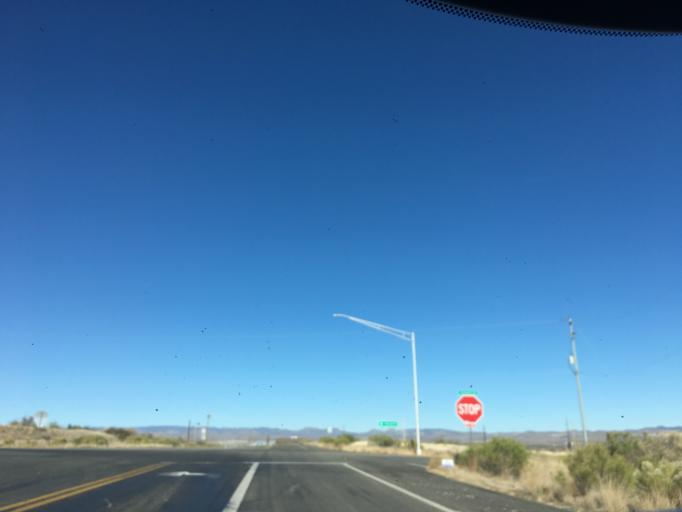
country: US
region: Arizona
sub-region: Yavapai County
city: Cordes Lakes
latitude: 34.3329
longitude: -112.1167
